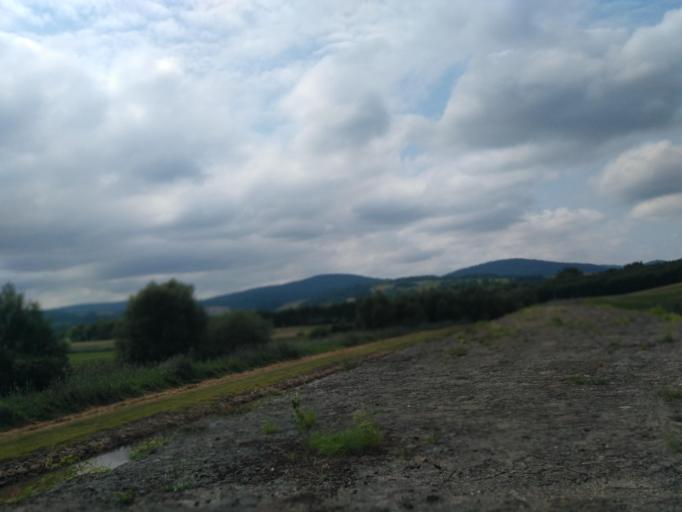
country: PL
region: Subcarpathian Voivodeship
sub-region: Powiat krosnienski
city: Rymanow
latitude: 49.5943
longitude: 21.8443
